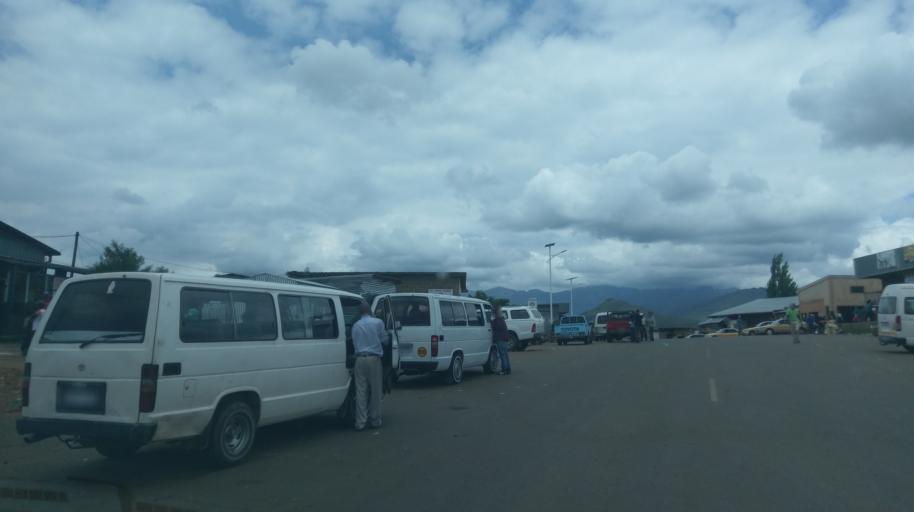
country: LS
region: Leribe
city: Leribe
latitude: -29.0007
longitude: 28.2093
